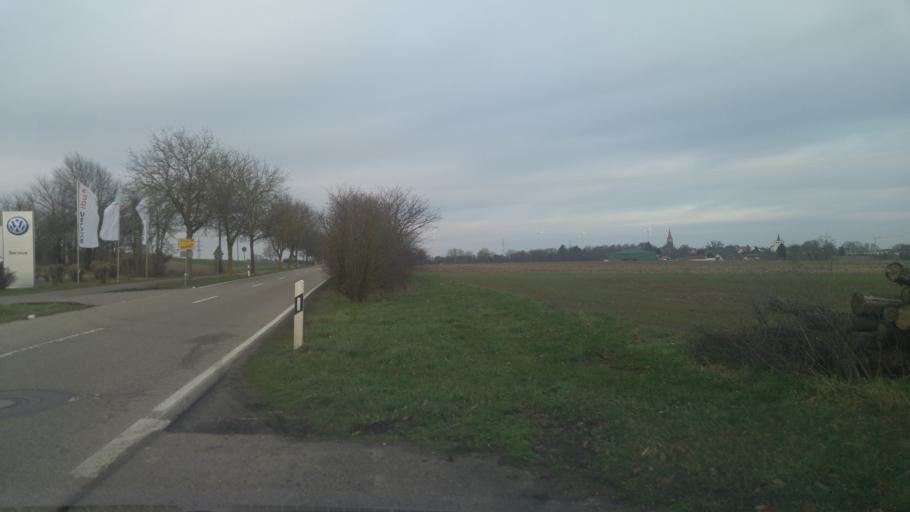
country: DE
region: Rheinland-Pfalz
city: Freckenfeld
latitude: 49.0684
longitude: 8.1262
